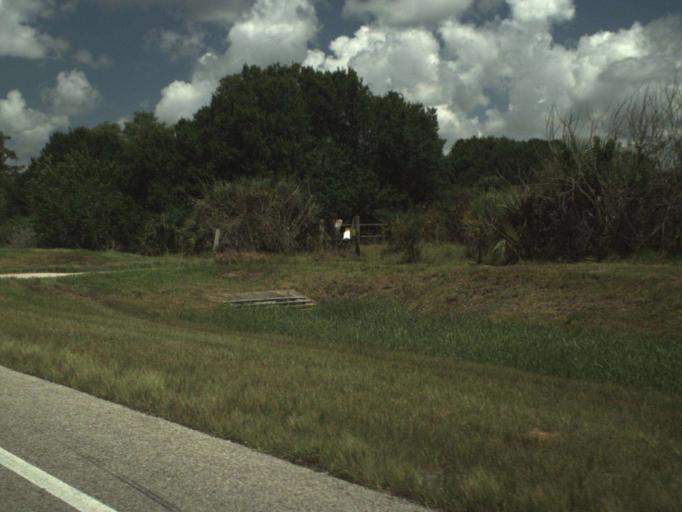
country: US
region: Florida
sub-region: Indian River County
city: West Vero Corridor
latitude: 27.6399
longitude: -80.5739
